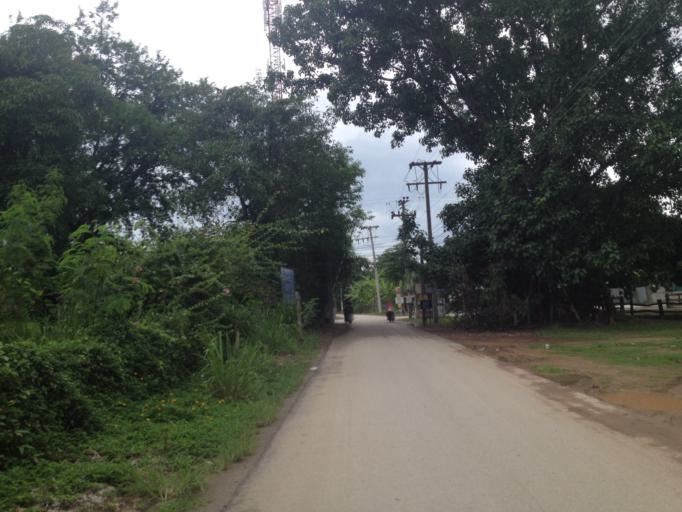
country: TH
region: Chiang Mai
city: Hang Dong
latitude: 18.6884
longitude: 98.8846
